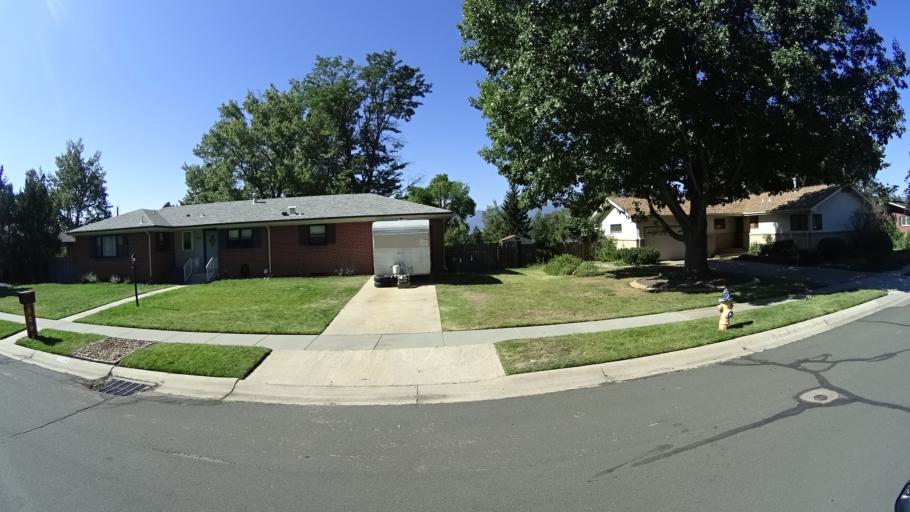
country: US
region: Colorado
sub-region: El Paso County
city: Colorado Springs
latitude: 38.8696
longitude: -104.7787
